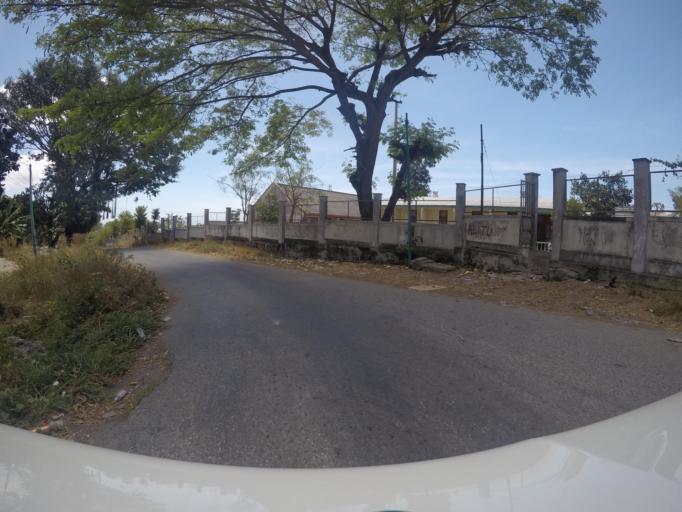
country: TL
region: Baucau
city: Baucau
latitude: -8.4649
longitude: 126.4610
